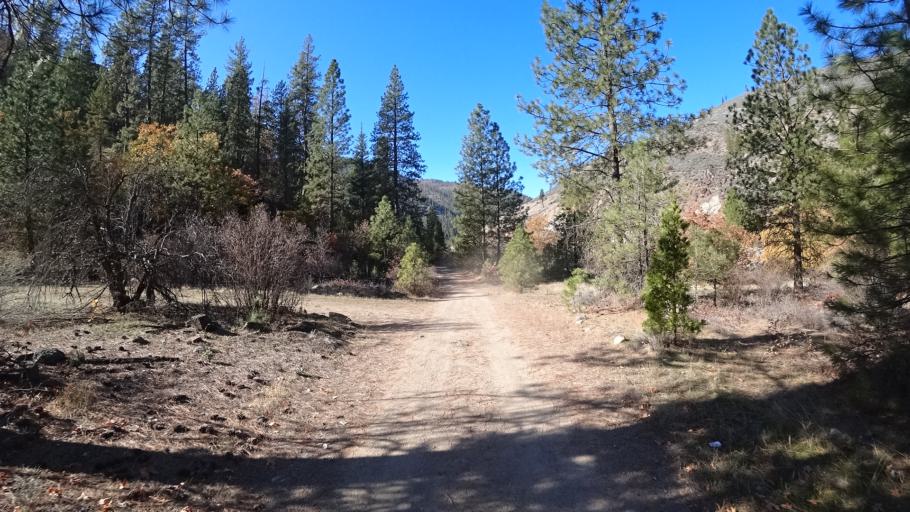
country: US
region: California
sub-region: Siskiyou County
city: Yreka
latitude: 41.8553
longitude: -122.7613
